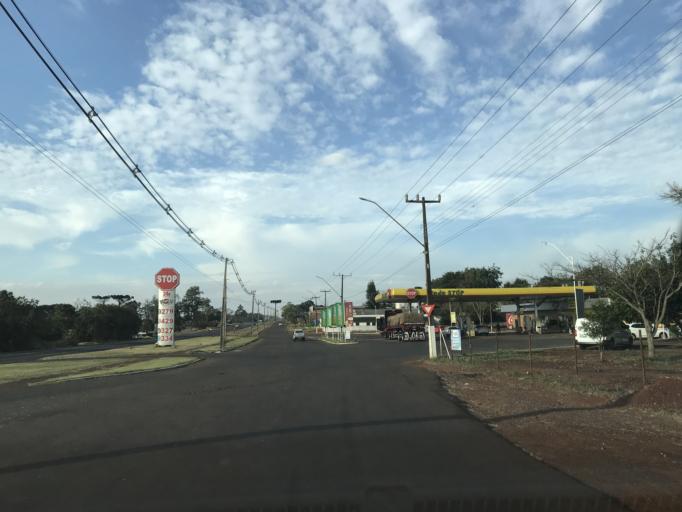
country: BR
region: Parana
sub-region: Cascavel
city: Cascavel
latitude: -25.0462
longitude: -53.6098
